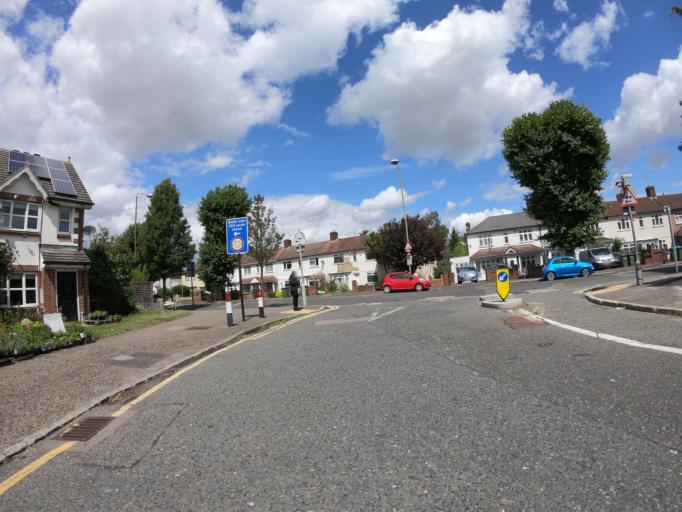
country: GB
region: England
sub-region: Greater London
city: Blackheath
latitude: 51.4871
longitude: 0.0151
